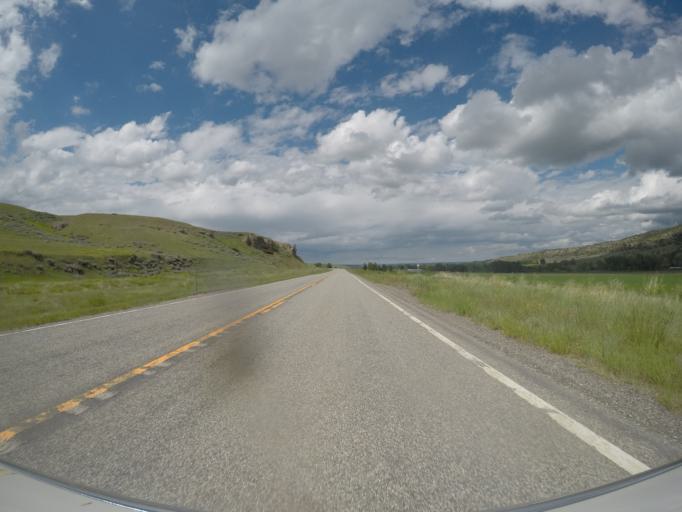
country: US
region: Montana
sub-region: Sweet Grass County
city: Big Timber
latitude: 45.7465
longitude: -109.9949
